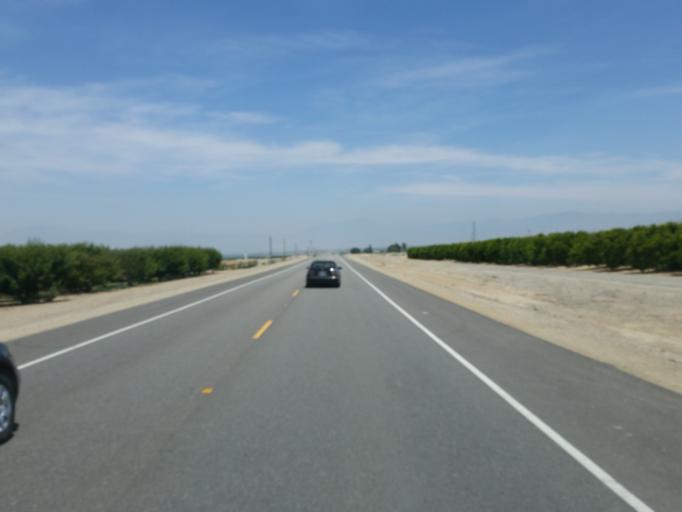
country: US
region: California
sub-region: Kern County
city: Pine Mountain Club
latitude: 35.0589
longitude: -119.0976
